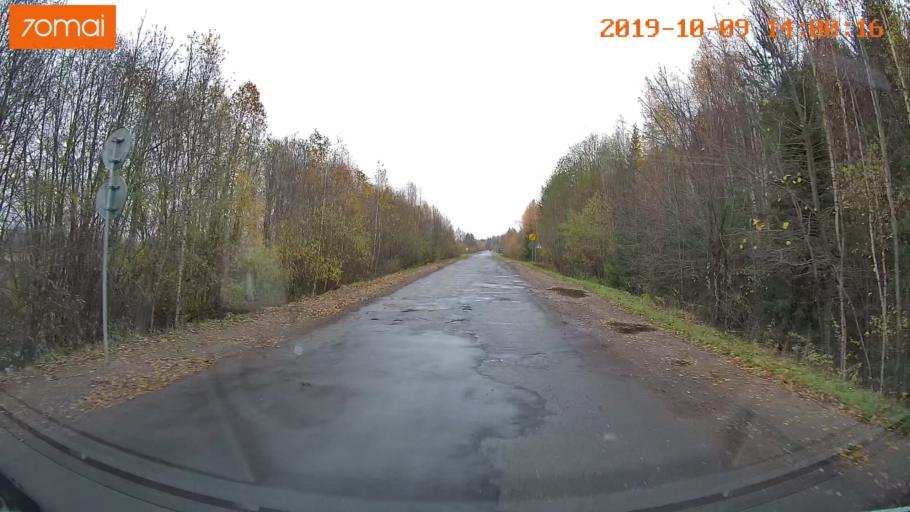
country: RU
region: Kostroma
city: Buy
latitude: 58.4387
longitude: 41.3339
